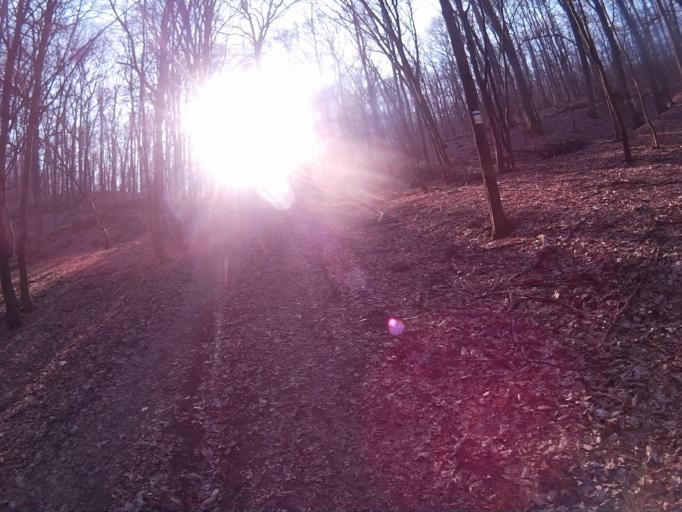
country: HU
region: Borsod-Abauj-Zemplen
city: Rudabanya
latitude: 48.4913
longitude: 20.5742
